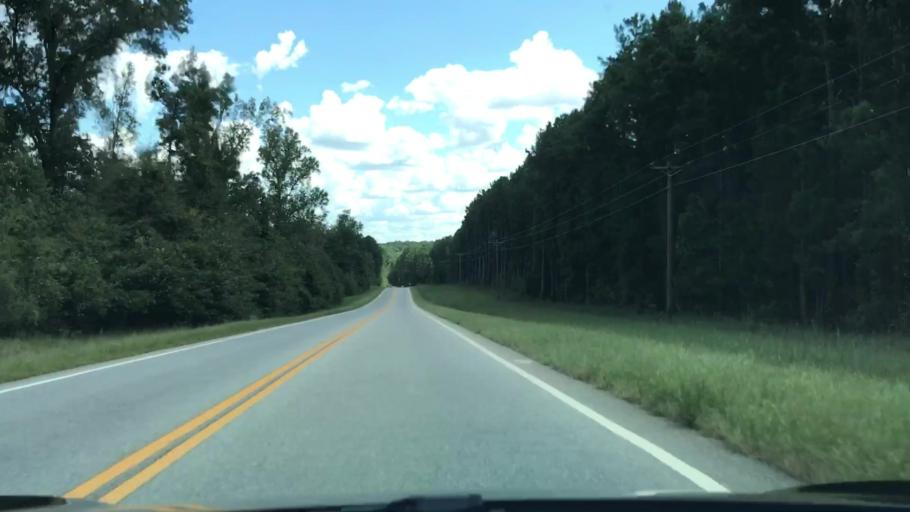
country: US
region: Georgia
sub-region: Greene County
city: Greensboro
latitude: 33.6779
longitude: -83.2694
